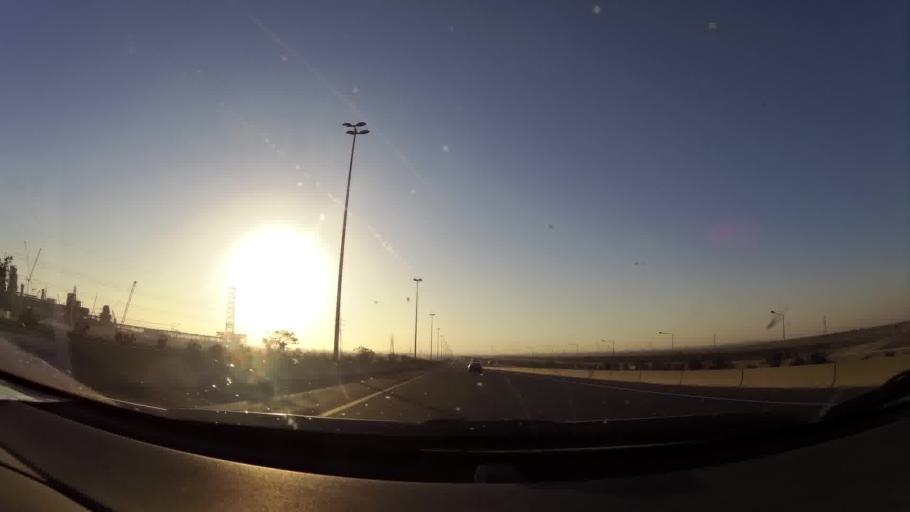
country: KW
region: Al Ahmadi
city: Al Fahahil
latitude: 28.9944
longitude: 48.1444
